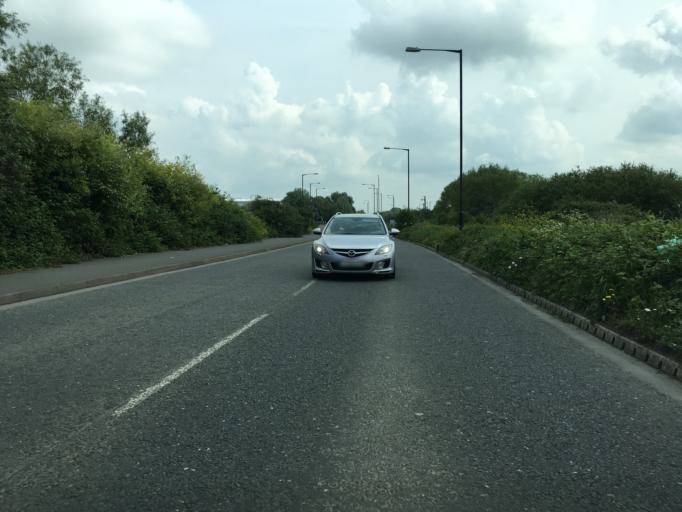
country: GB
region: England
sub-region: South Gloucestershire
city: Severn Beach
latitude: 51.5173
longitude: -2.6778
